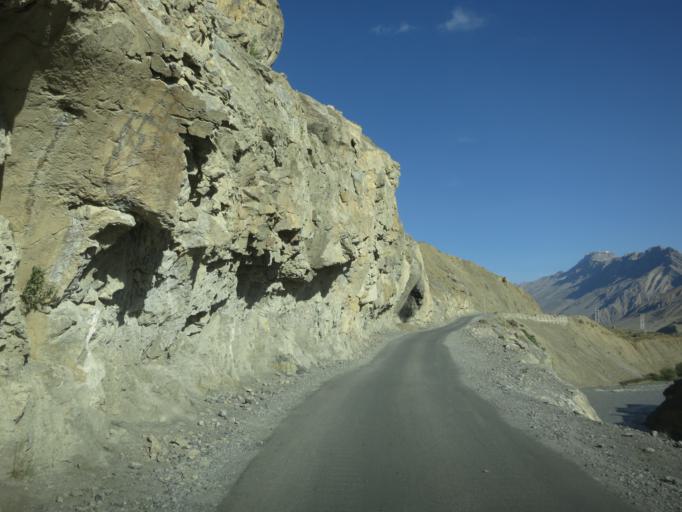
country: IN
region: Himachal Pradesh
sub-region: Shimla
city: Sarahan
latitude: 32.2468
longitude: 78.0528
